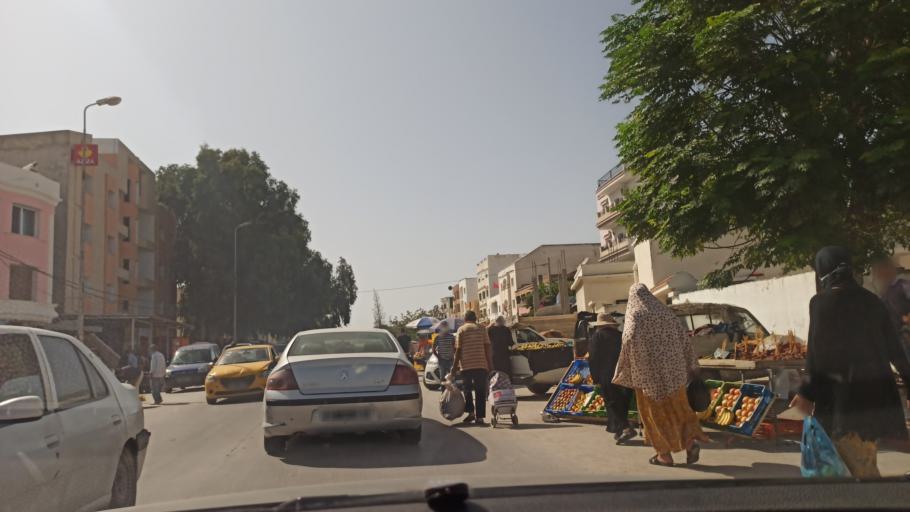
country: TN
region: Manouba
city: Manouba
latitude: 36.7671
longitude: 10.1114
